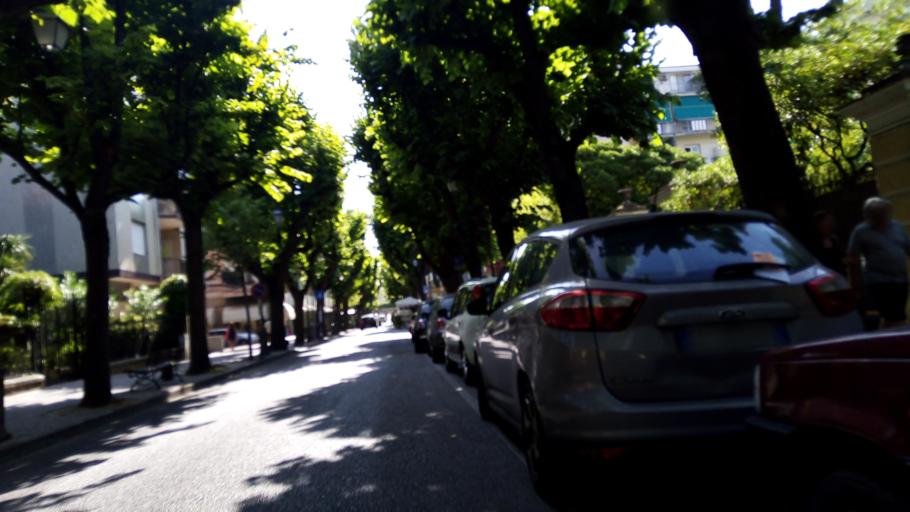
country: IT
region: Liguria
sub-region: Provincia di Savona
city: Albenga
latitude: 44.0475
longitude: 8.2174
